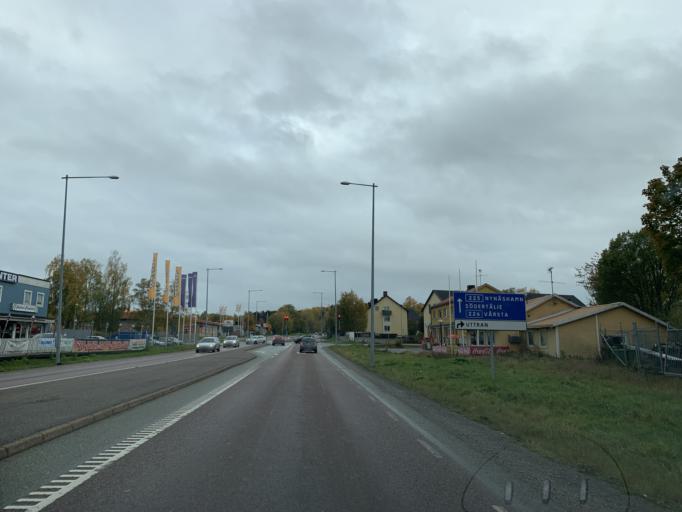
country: SE
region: Stockholm
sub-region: Botkyrka Kommun
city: Tumba
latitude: 59.1913
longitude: 17.8229
